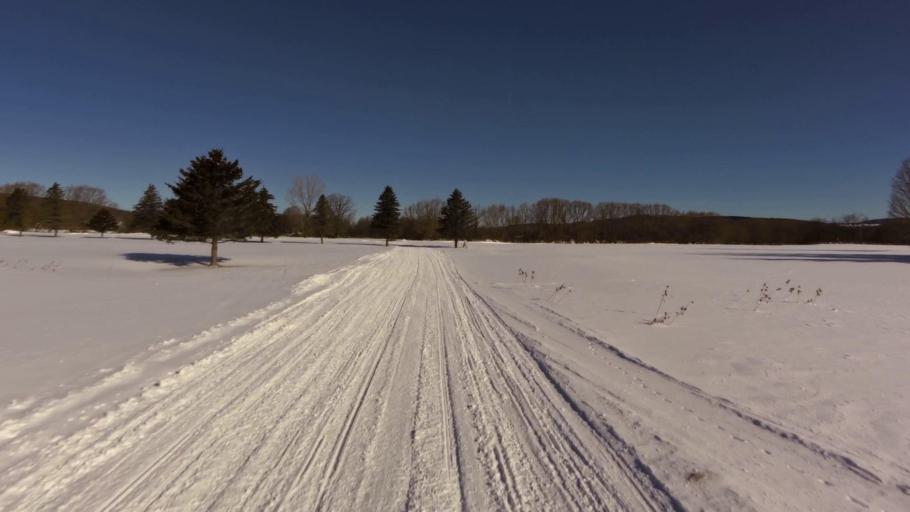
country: US
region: New York
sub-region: Cattaraugus County
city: Franklinville
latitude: 42.3596
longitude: -78.4567
